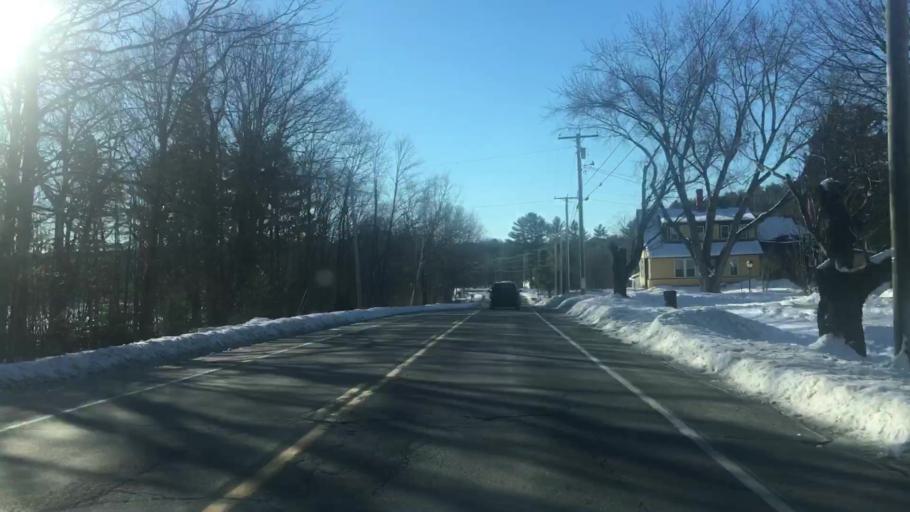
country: US
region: Maine
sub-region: Somerset County
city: Madison
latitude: 44.8166
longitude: -69.8864
